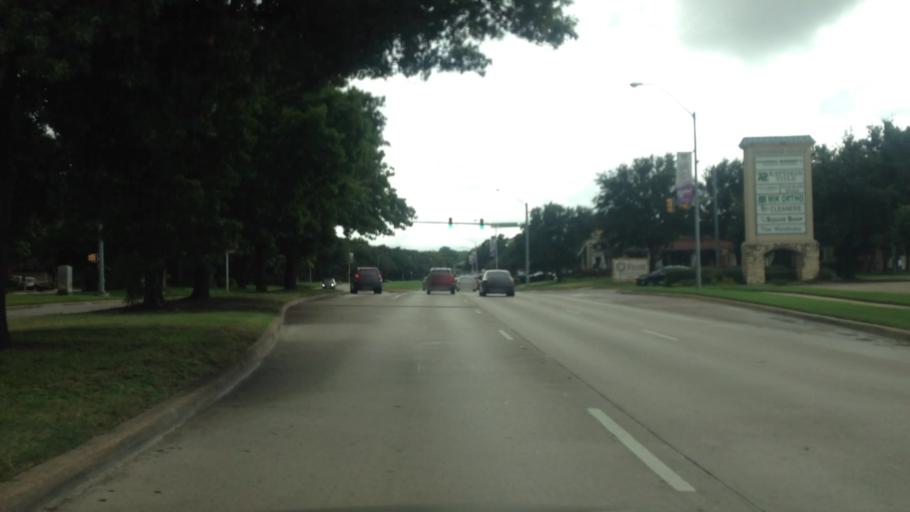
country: US
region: Texas
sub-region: Tarrant County
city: Westworth
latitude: 32.7091
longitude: -97.3870
